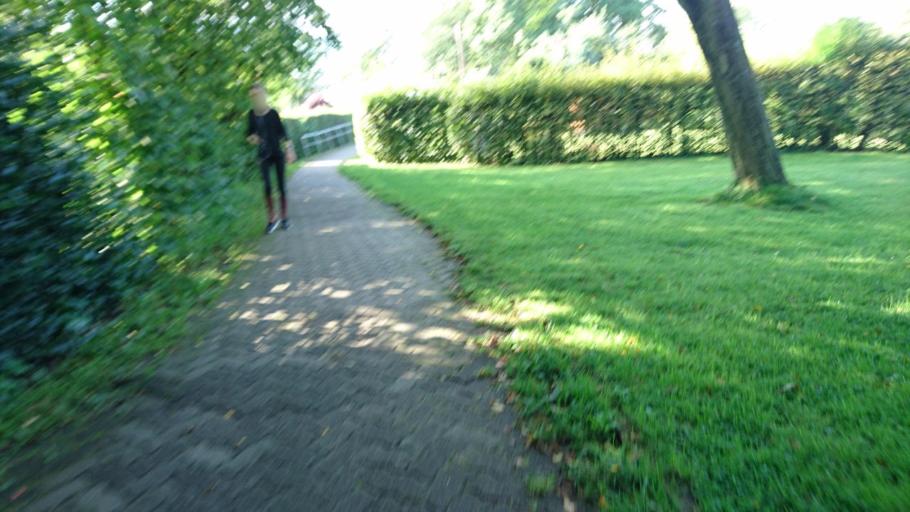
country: DE
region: Hamburg
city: Winterhude
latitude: 53.6066
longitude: 9.9956
